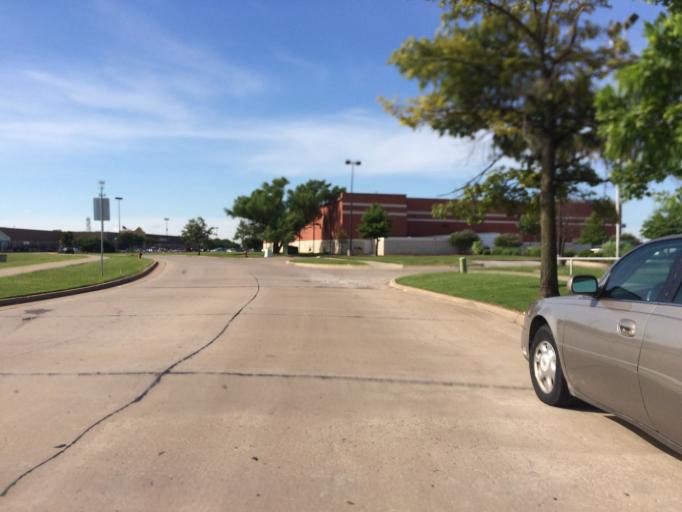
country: US
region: Oklahoma
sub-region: Cleveland County
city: Norman
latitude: 35.2237
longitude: -97.4829
